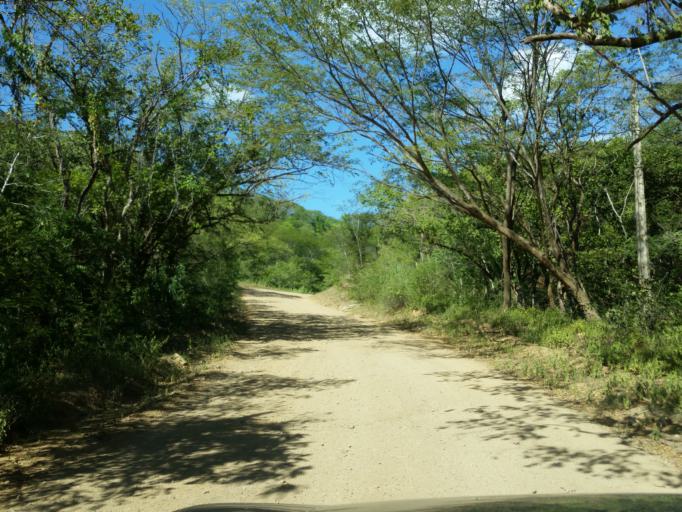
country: NI
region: Rivas
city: San Juan del Sur
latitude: 11.1619
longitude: -85.8001
